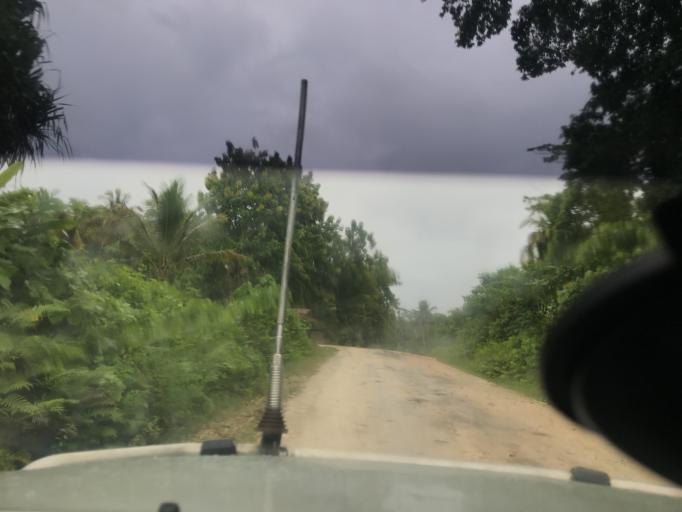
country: SB
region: Malaita
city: Auki
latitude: -9.0054
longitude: 160.7936
